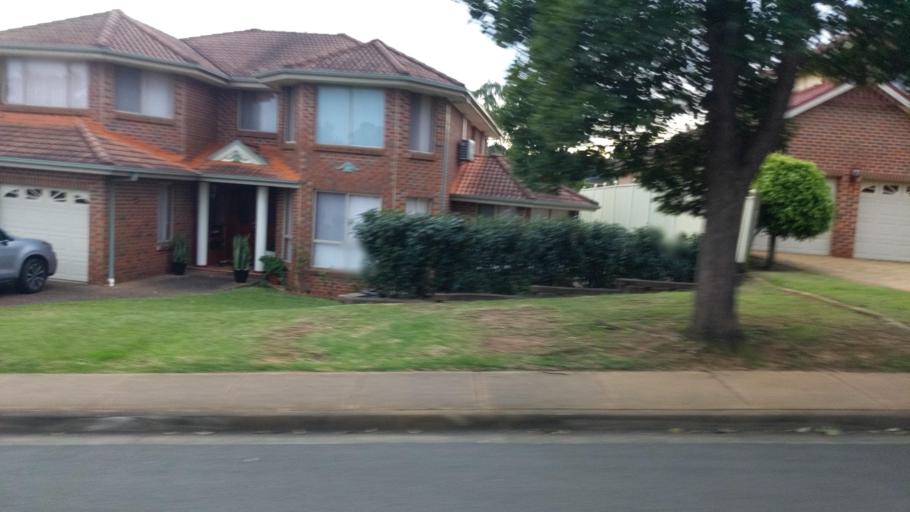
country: AU
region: New South Wales
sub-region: The Hills Shire
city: Baulkham Hills
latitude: -33.7447
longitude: 150.9611
